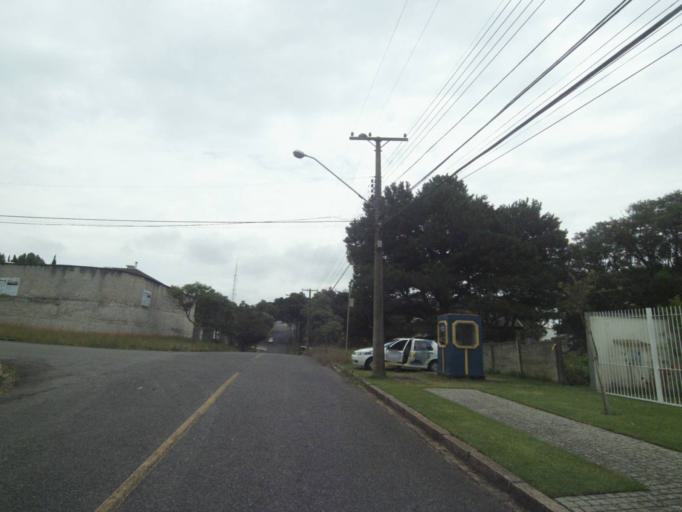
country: BR
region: Parana
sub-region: Curitiba
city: Curitiba
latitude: -25.4042
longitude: -49.2862
